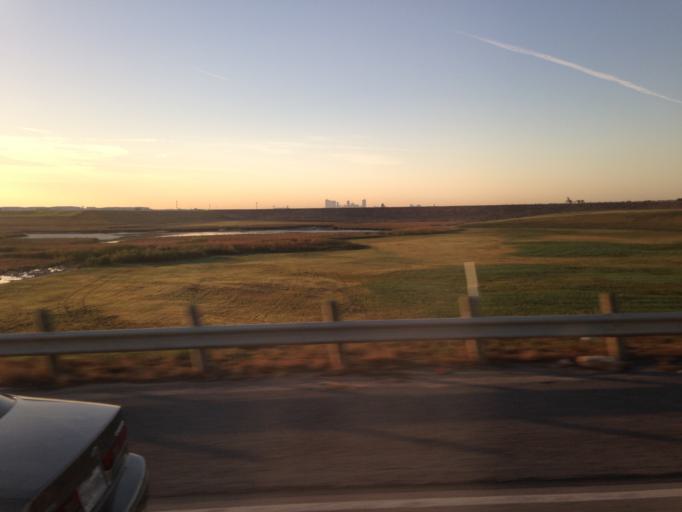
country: US
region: Texas
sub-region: Tarrant County
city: Saginaw
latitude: 32.8337
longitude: -97.3699
